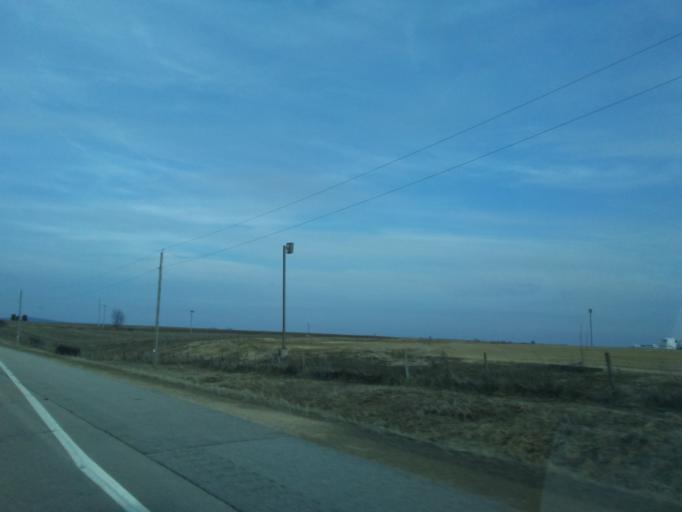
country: US
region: Wisconsin
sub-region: Iowa County
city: Dodgeville
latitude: 42.9767
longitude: -90.0229
